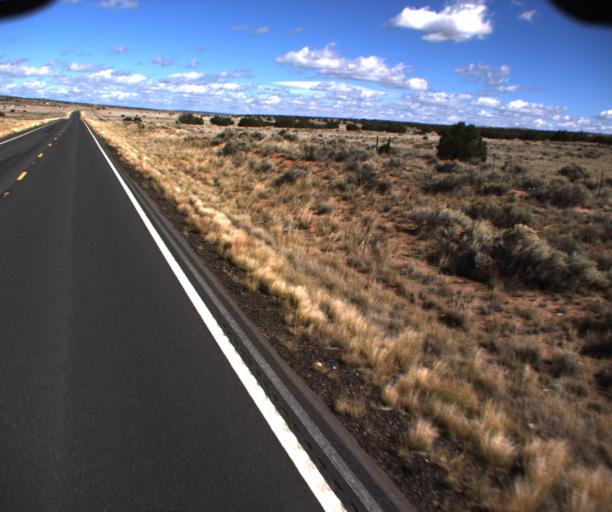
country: US
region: Arizona
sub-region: Apache County
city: Houck
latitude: 34.9142
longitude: -109.2382
